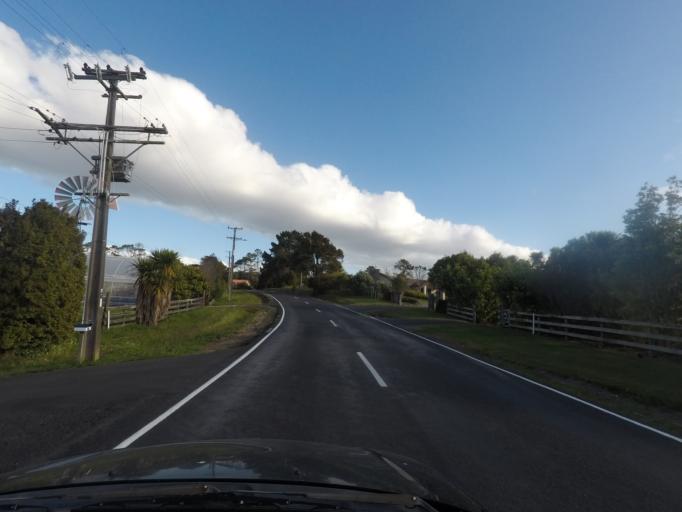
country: NZ
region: Auckland
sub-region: Auckland
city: Waitakere
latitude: -36.9177
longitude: 174.6151
